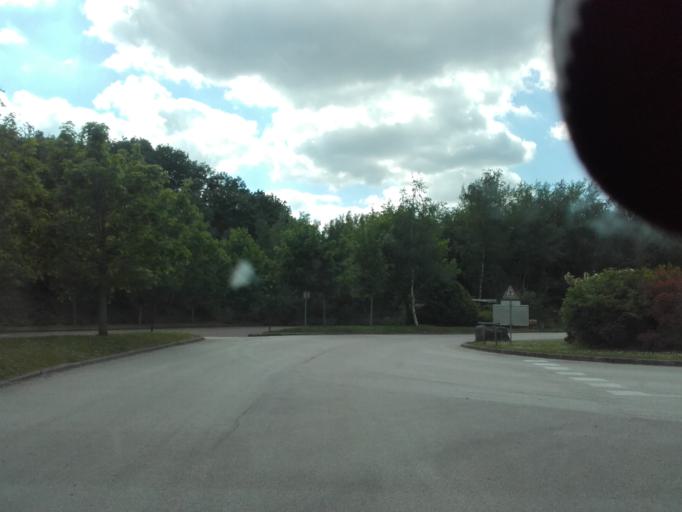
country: FR
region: Bourgogne
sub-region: Departement de Saone-et-Loire
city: Fontaines
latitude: 46.8863
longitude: 4.7860
